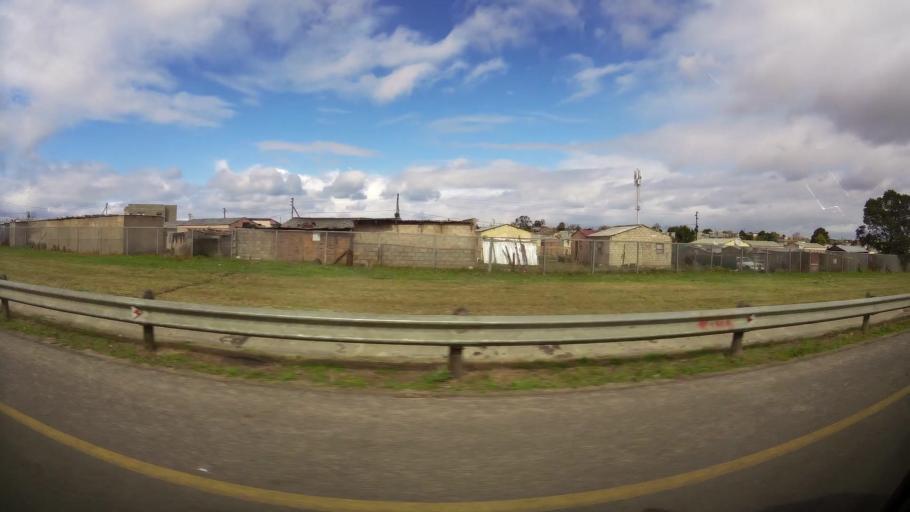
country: ZA
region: Western Cape
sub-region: Eden District Municipality
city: George
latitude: -33.9961
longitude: 22.4723
